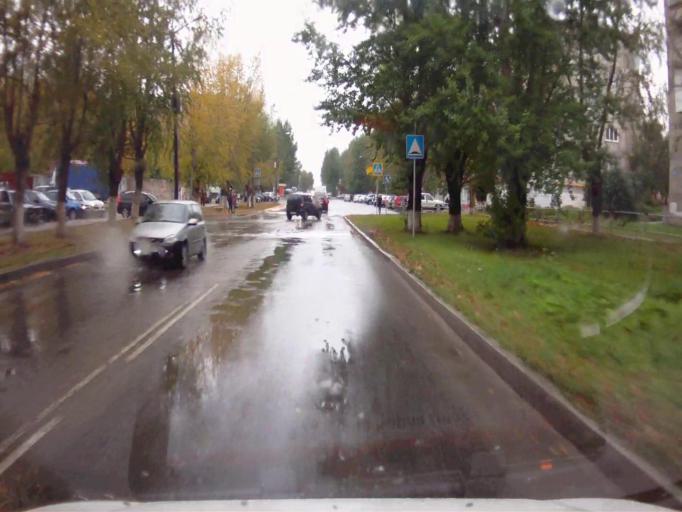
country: RU
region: Chelyabinsk
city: Kyshtym
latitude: 55.7014
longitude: 60.5558
